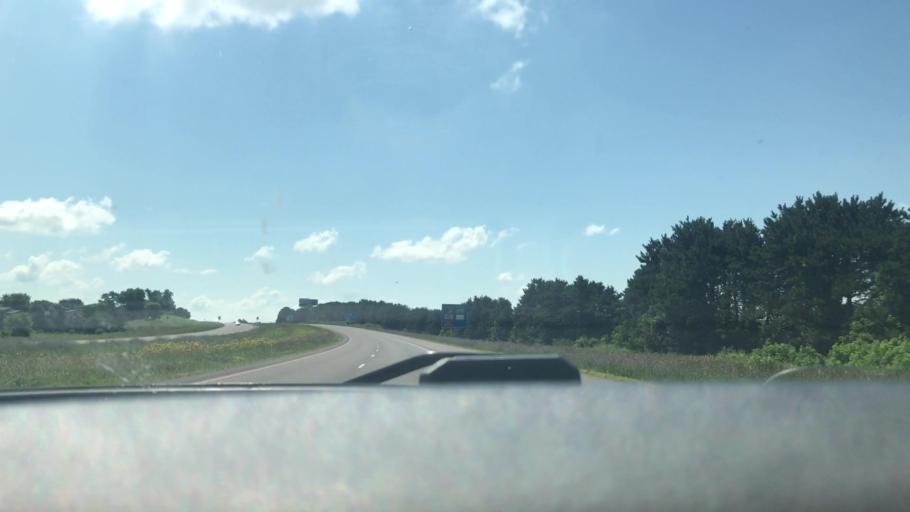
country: US
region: Wisconsin
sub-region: Chippewa County
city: Bloomer
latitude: 45.1078
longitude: -91.5153
